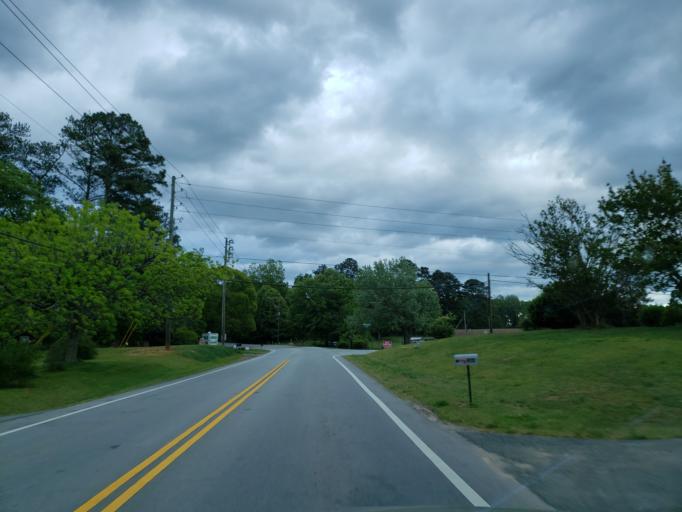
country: US
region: Georgia
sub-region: Paulding County
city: Hiram
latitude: 33.8660
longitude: -84.8038
